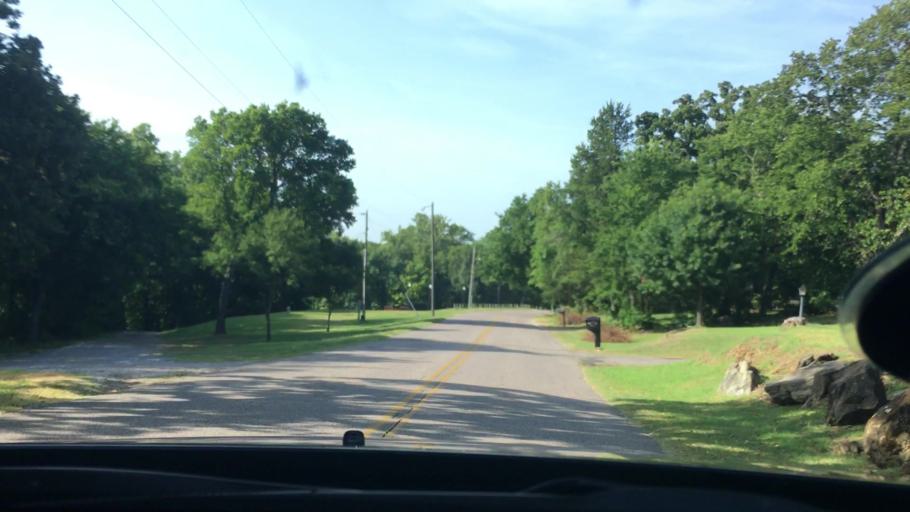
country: US
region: Oklahoma
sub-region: Pontotoc County
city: Ada
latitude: 34.7598
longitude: -96.6553
